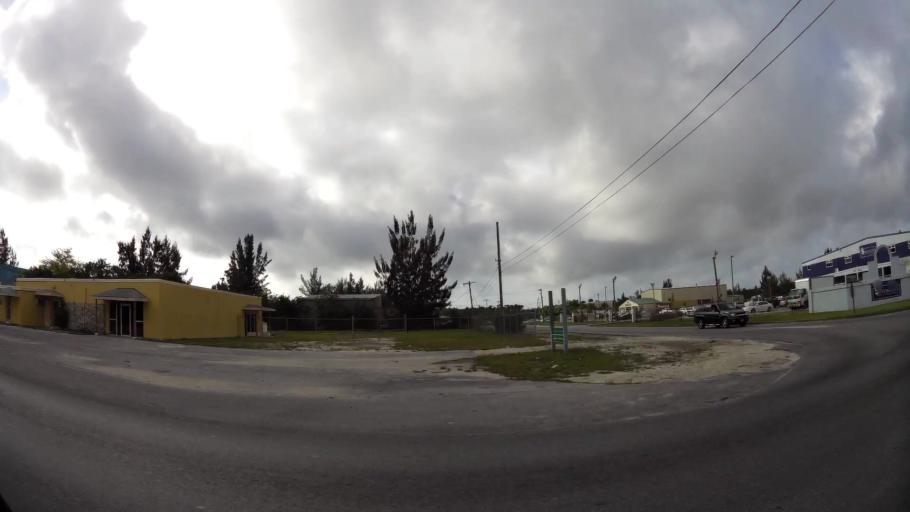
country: BS
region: Freeport
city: Freeport
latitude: 26.5395
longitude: -78.7103
